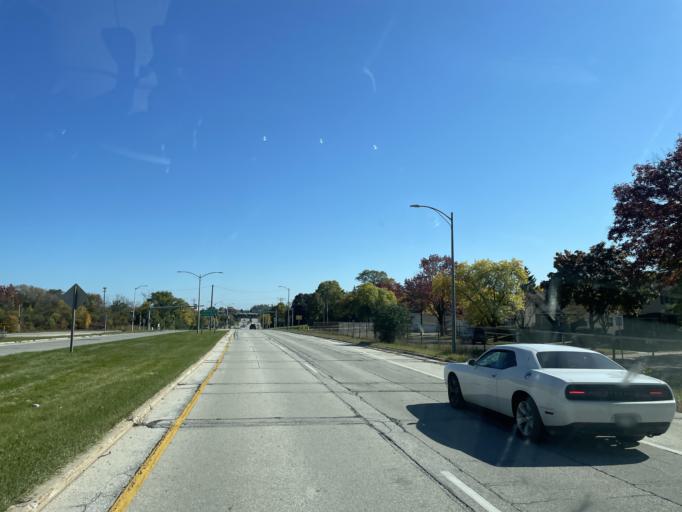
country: US
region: Wisconsin
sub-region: Waukesha County
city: Butler
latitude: 43.1281
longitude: -88.0469
